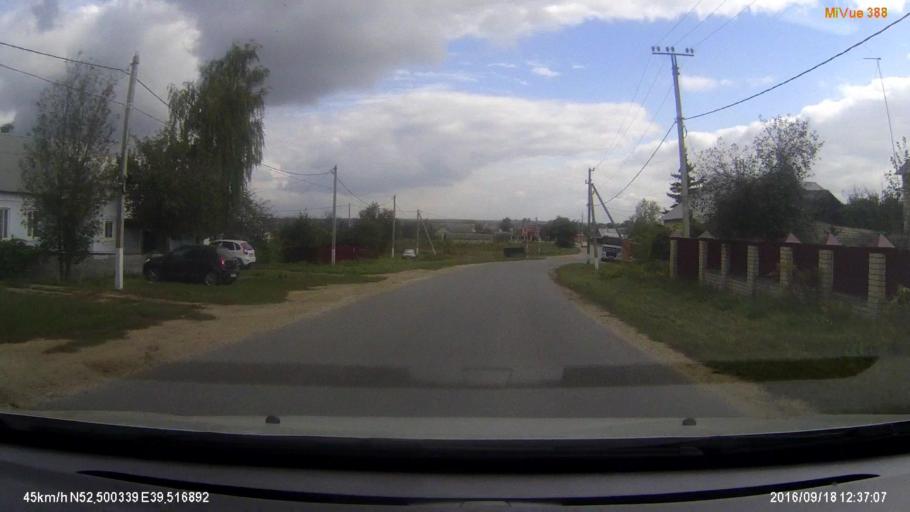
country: RU
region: Lipetsk
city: Syrskoye
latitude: 52.5002
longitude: 39.5175
